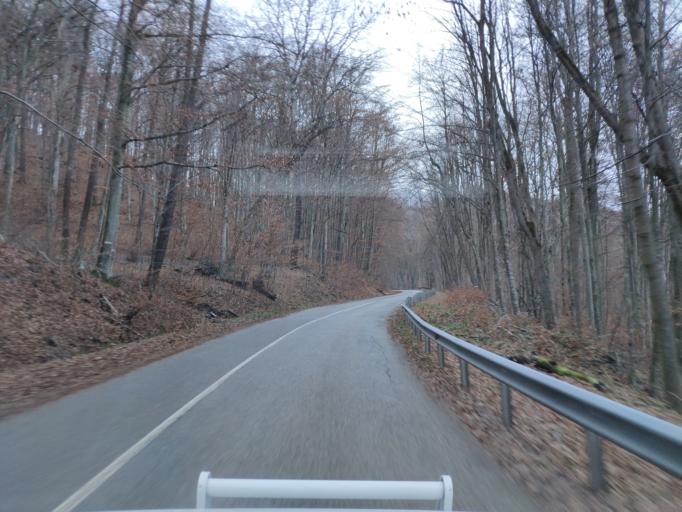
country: SK
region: Kosicky
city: Dobsina
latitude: 48.7755
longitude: 20.4742
